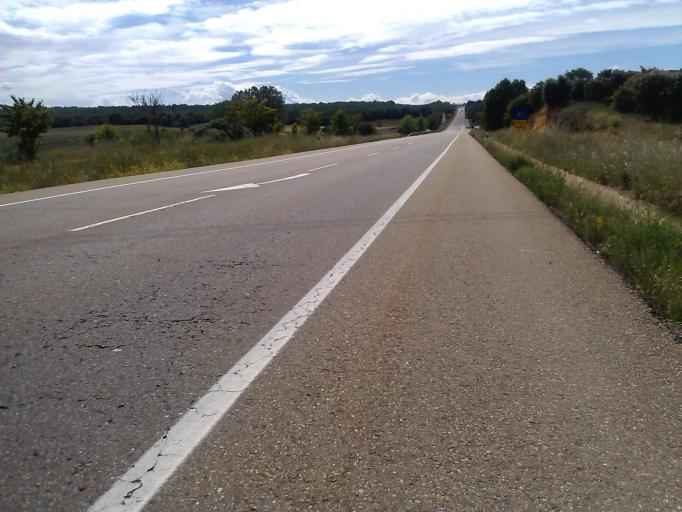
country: ES
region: Castille and Leon
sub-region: Provincia de Leon
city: Villares de Orbigo
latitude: 42.4474
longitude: -5.9608
